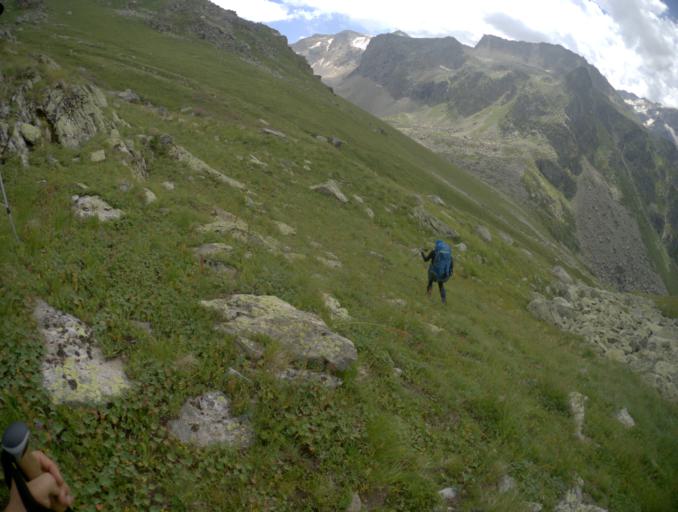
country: RU
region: Karachayevo-Cherkesiya
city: Uchkulan
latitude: 43.2944
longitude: 42.0779
